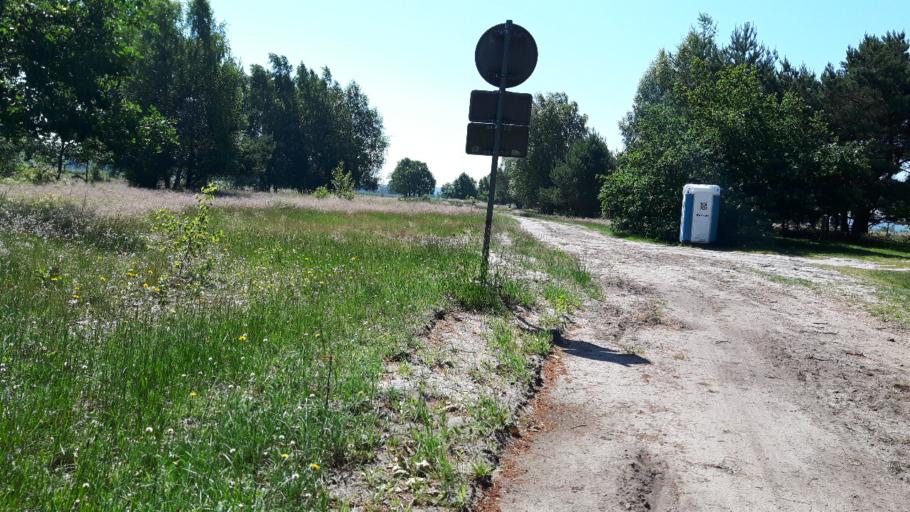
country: PL
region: Pomeranian Voivodeship
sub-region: Powiat slupski
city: Smoldzino
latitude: 54.6750
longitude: 17.1574
